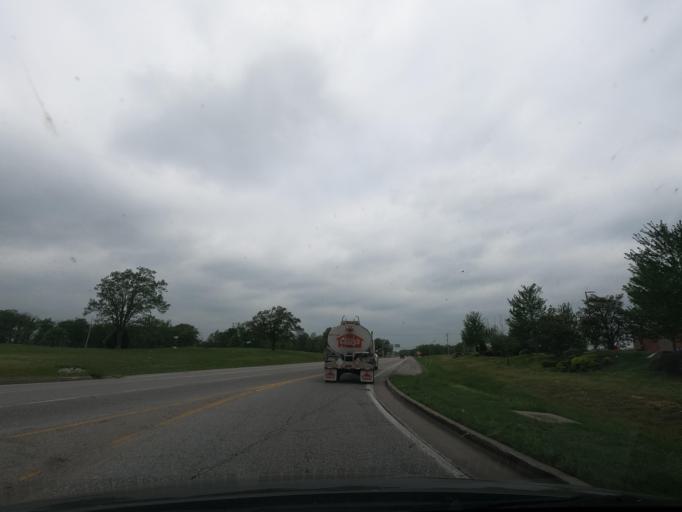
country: US
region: Kansas
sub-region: Cherokee County
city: Galena
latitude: 37.0023
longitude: -94.6157
